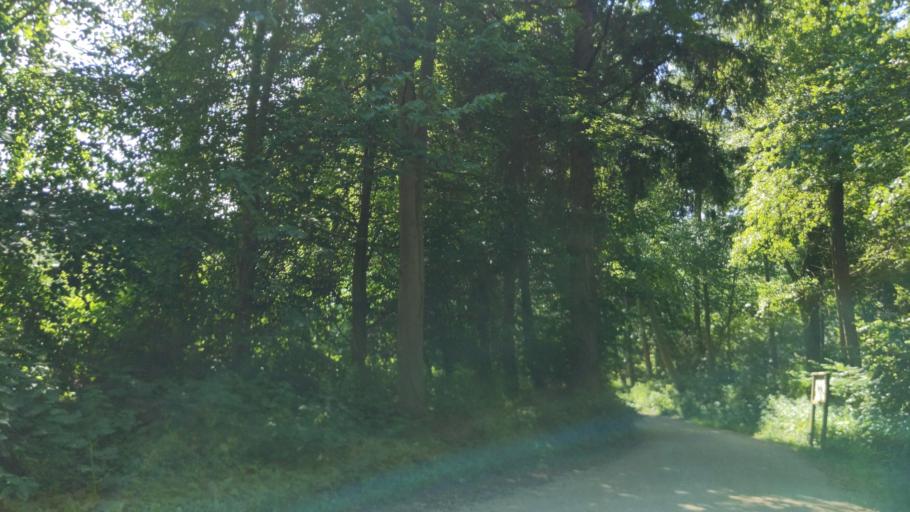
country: DE
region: Schleswig-Holstein
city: Ploen
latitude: 54.1483
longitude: 10.4086
